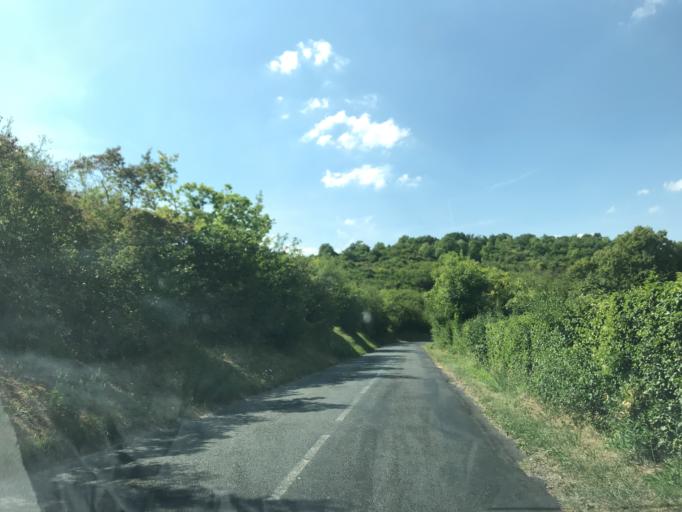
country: FR
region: Ile-de-France
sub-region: Departement des Yvelines
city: Freneuse
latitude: 49.0627
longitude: 1.6002
